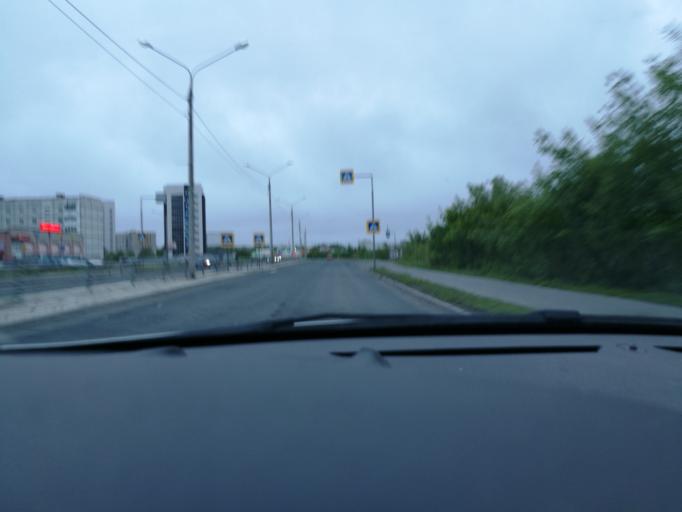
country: RU
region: Arkhangelskaya
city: Severodvinsk
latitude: 64.5609
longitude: 39.7796
